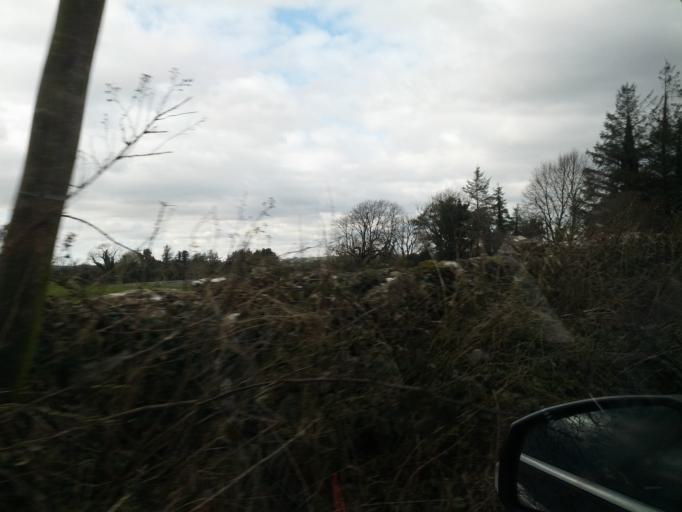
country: IE
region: Connaught
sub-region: County Galway
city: Athenry
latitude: 53.3888
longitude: -8.6608
